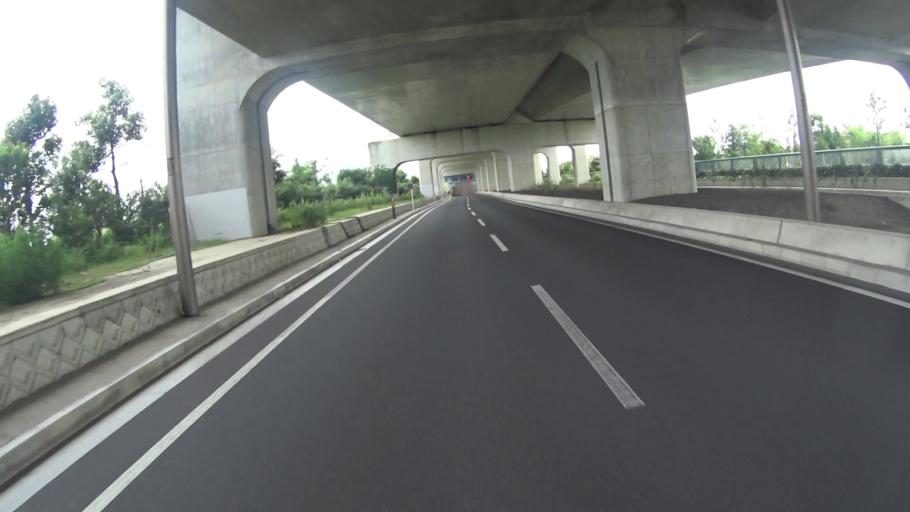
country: JP
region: Kyoto
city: Yawata
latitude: 34.8911
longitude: 135.7495
